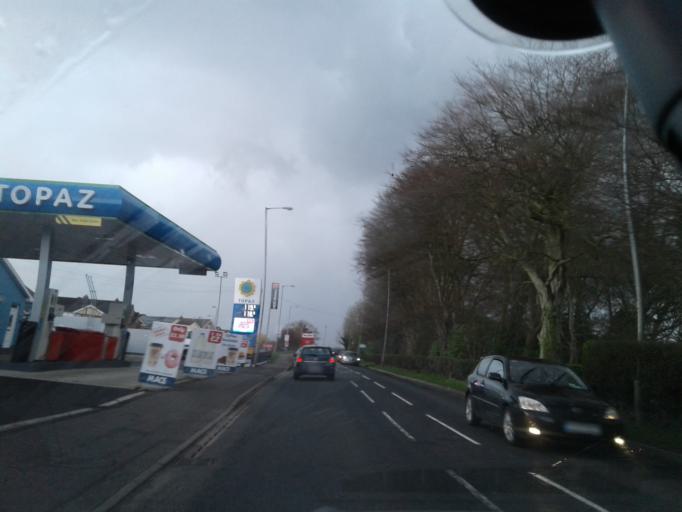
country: GB
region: Northern Ireland
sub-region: Strabane District
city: Sion Mills
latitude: 54.7904
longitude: -7.4738
